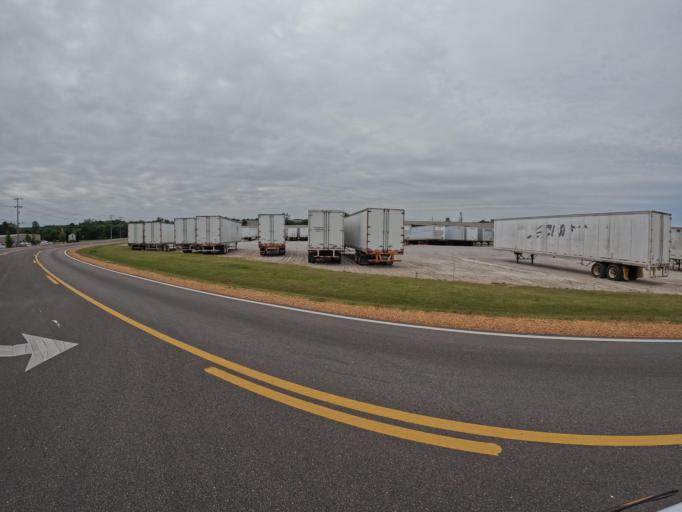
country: US
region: Mississippi
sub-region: Lee County
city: Tupelo
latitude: 34.2815
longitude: -88.7654
